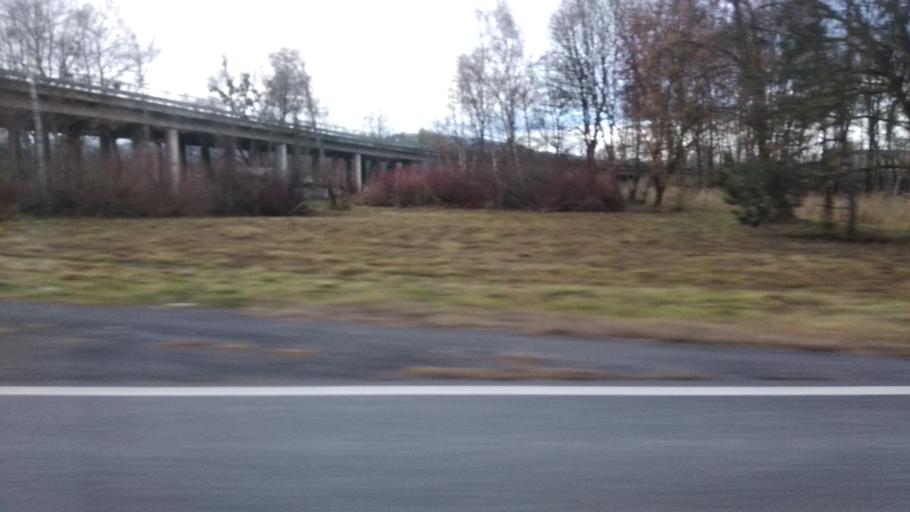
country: AT
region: Vorarlberg
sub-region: Politischer Bezirk Bregenz
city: Wolfurt
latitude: 47.4453
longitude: 9.7230
